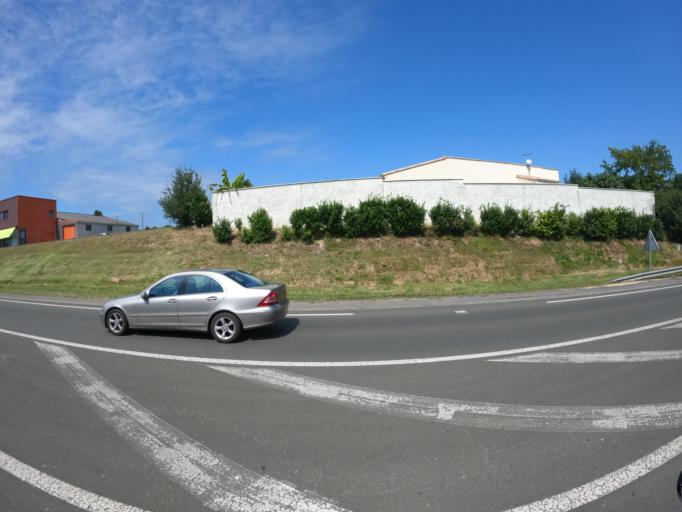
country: FR
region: Poitou-Charentes
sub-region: Departement des Deux-Sevres
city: Bessines
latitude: 46.2977
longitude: -0.4988
